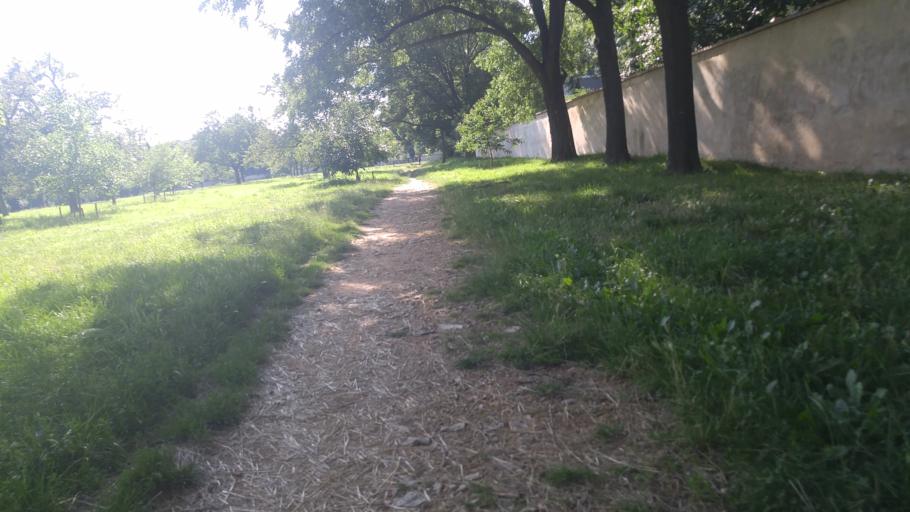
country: CZ
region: Praha
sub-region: Praha 1
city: Mala Strana
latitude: 50.0874
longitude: 14.3568
